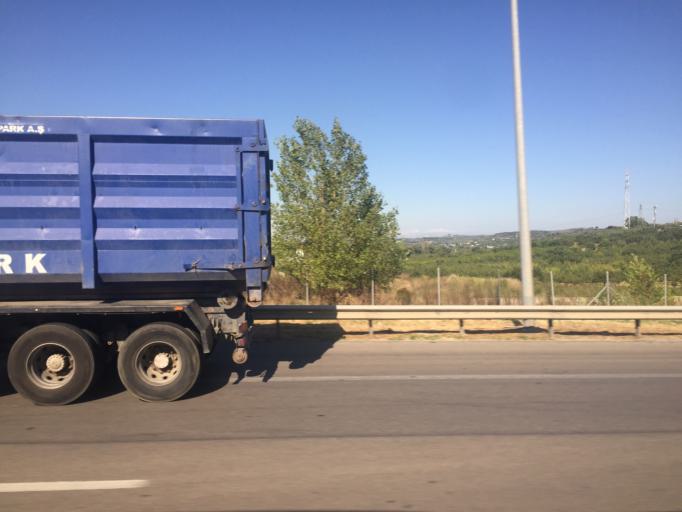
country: TR
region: Bursa
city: Demirtas
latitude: 40.2832
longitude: 29.0407
